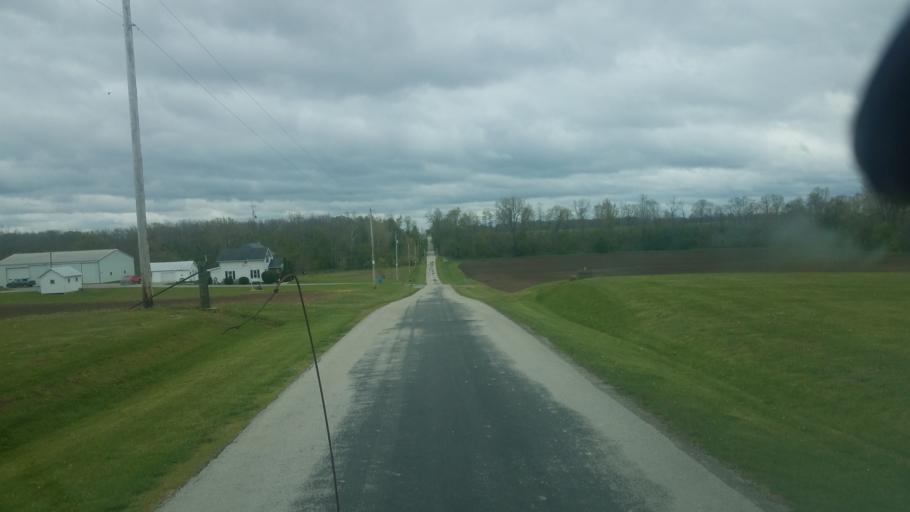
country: US
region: Ohio
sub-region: Wyandot County
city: Upper Sandusky
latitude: 40.7643
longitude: -83.1450
